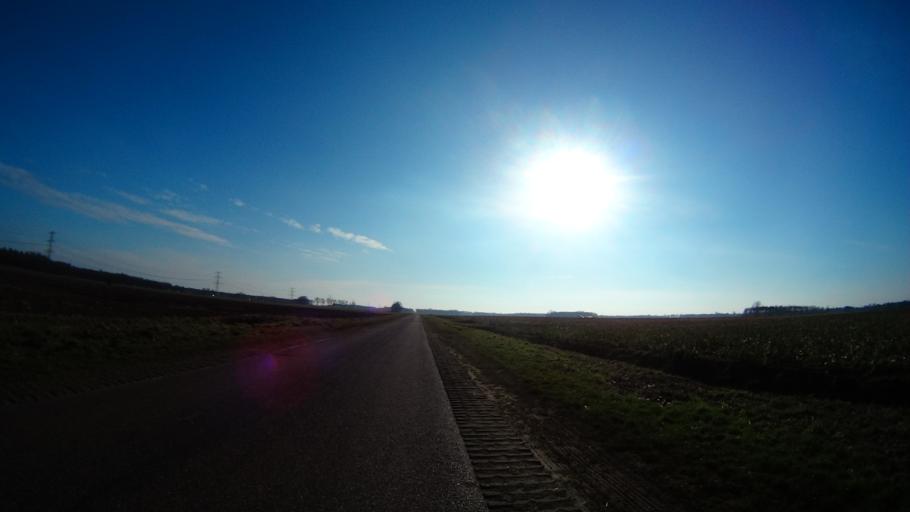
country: NL
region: Drenthe
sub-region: Gemeente Coevorden
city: Sleen
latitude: 52.7774
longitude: 6.8397
